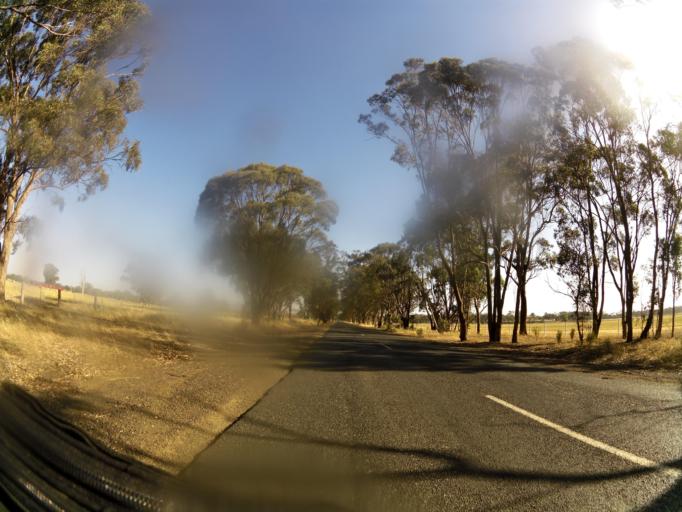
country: AU
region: Victoria
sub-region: Murrindindi
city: Kinglake West
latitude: -36.9785
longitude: 145.1104
